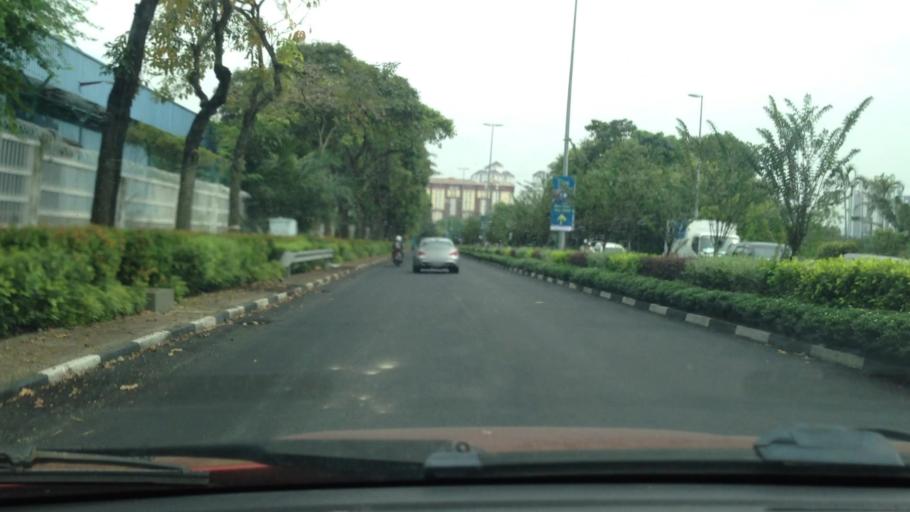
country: MY
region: Selangor
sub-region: Petaling
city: Petaling Jaya
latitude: 3.0901
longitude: 101.6070
